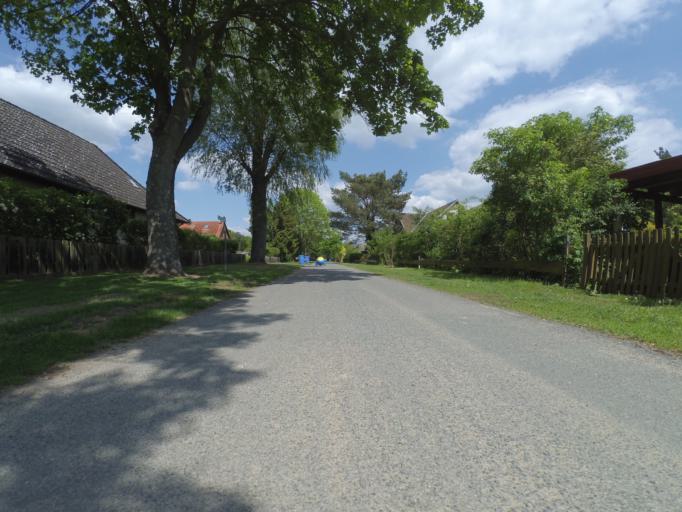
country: DE
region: Lower Saxony
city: Meinersen
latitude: 52.4610
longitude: 10.3265
